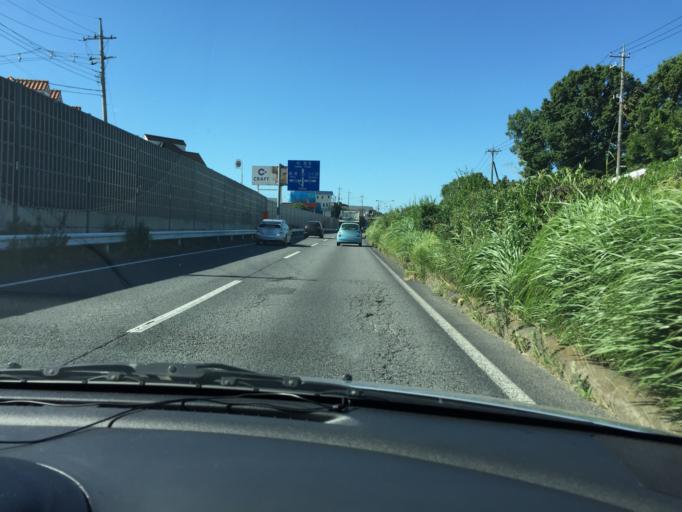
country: JP
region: Ibaraki
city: Naka
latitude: 36.0637
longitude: 140.1790
